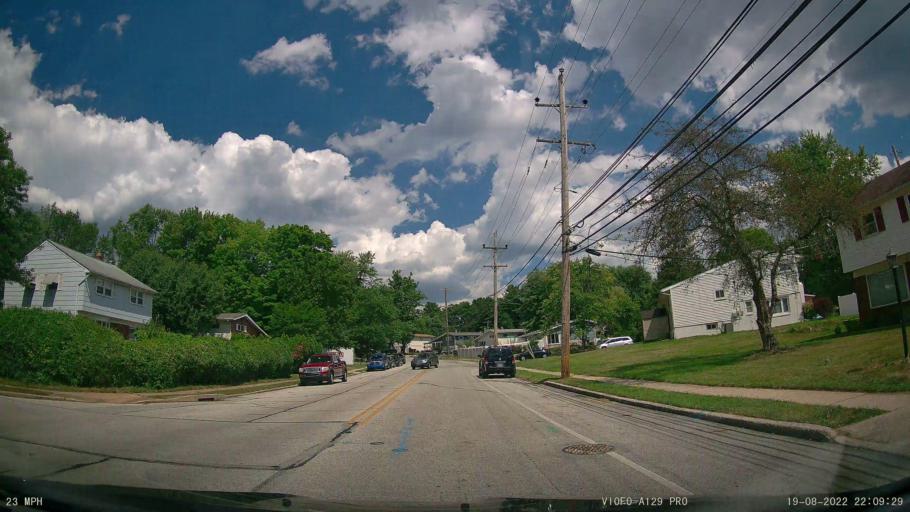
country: US
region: Pennsylvania
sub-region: Montgomery County
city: King of Prussia
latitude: 40.1009
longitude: -75.3805
